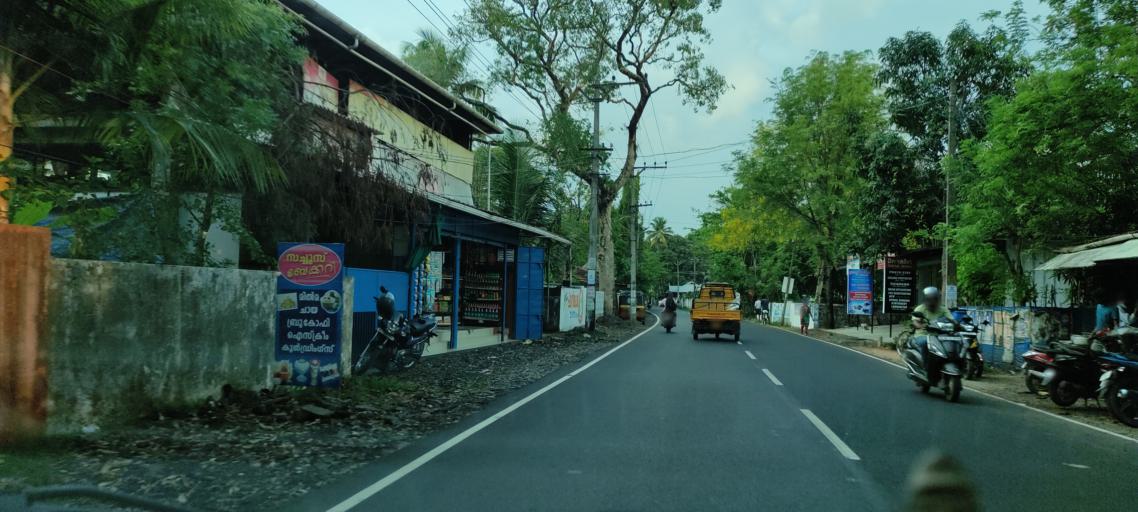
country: IN
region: Kerala
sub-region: Alappuzha
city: Kutiatodu
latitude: 9.8296
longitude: 76.3412
